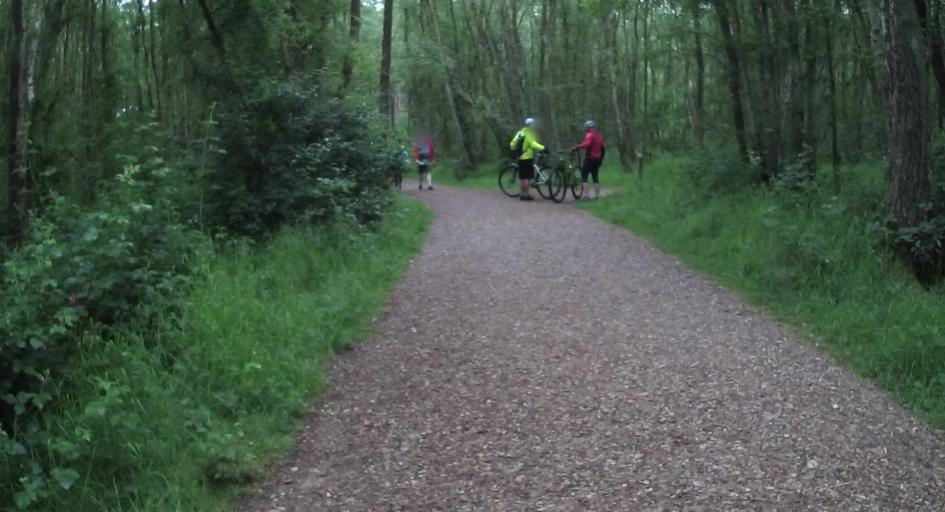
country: GB
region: England
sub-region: Hampshire
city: Farnborough
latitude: 51.2874
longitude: -0.7895
